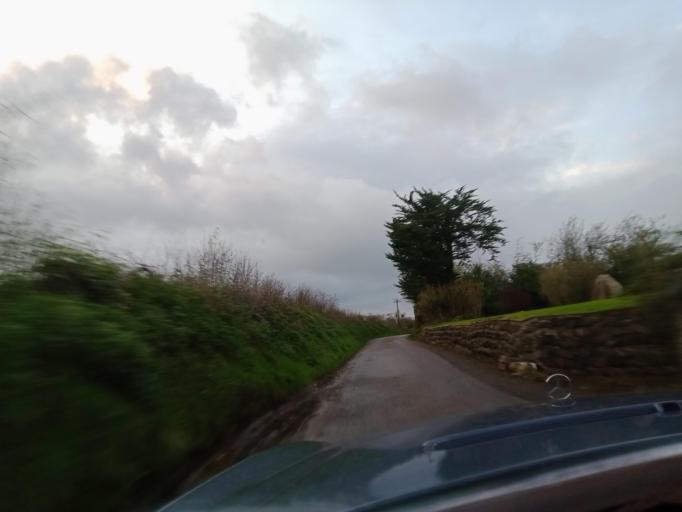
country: IE
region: Leinster
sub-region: Loch Garman
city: New Ross
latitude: 52.3317
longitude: -7.0269
